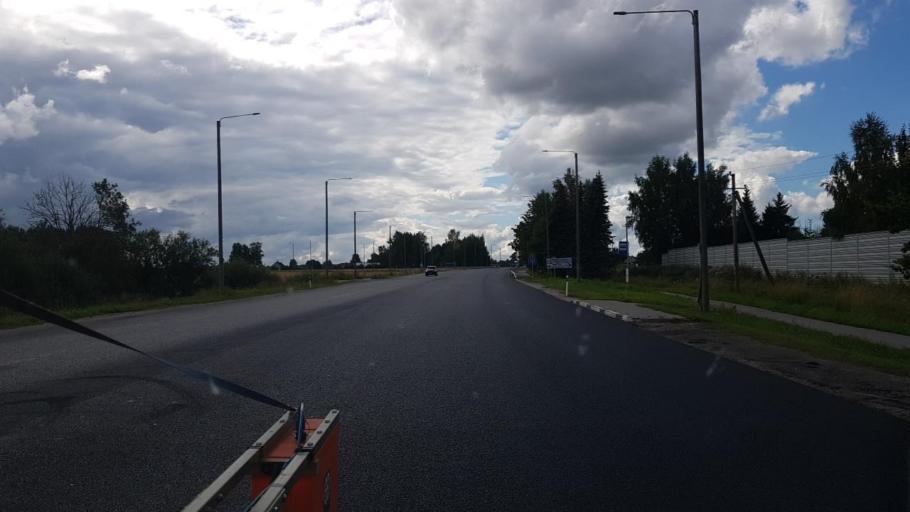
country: EE
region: Tartu
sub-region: UElenurme vald
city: Ulenurme
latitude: 58.2966
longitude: 26.7174
